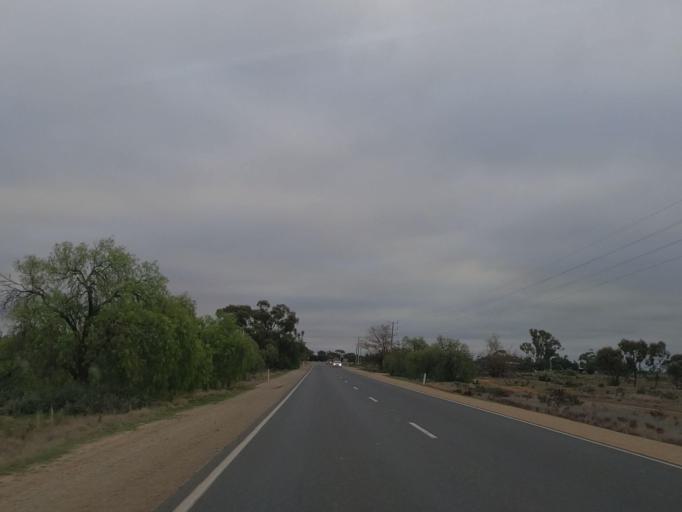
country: AU
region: Victoria
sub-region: Swan Hill
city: Swan Hill
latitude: -35.4442
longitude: 143.6182
